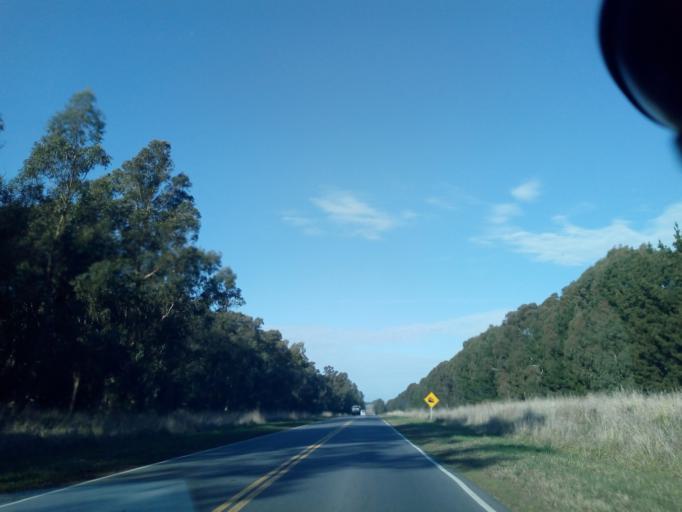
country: AR
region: Buenos Aires
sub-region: Partido de Tandil
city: Tandil
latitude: -37.3536
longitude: -58.8814
